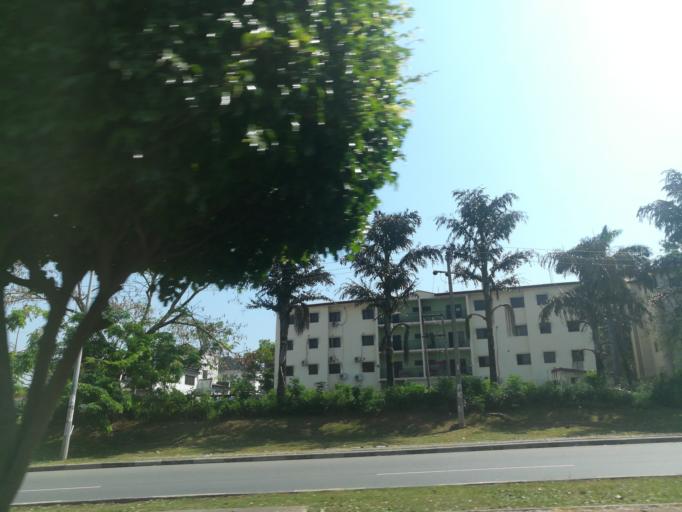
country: NG
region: Abuja Federal Capital Territory
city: Abuja
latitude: 9.0566
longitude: 7.4594
